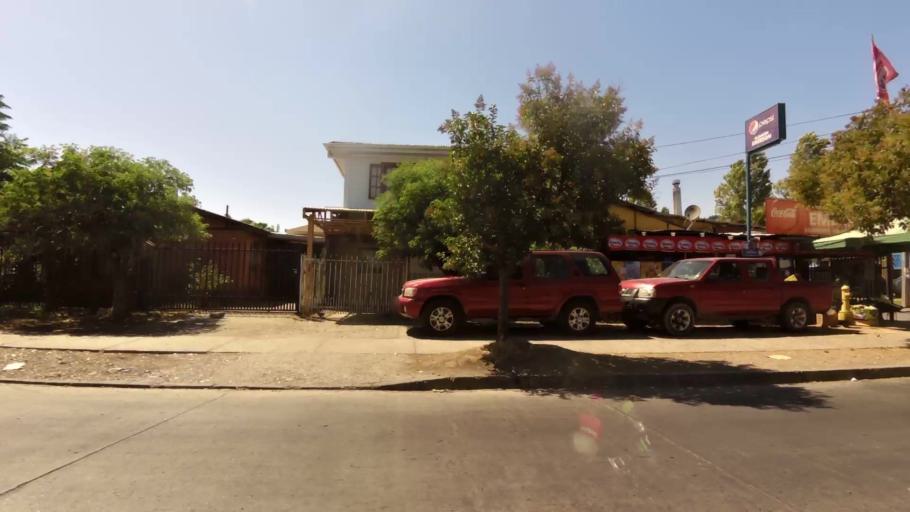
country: CL
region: Maule
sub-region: Provincia de Curico
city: Curico
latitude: -34.9739
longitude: -71.2351
